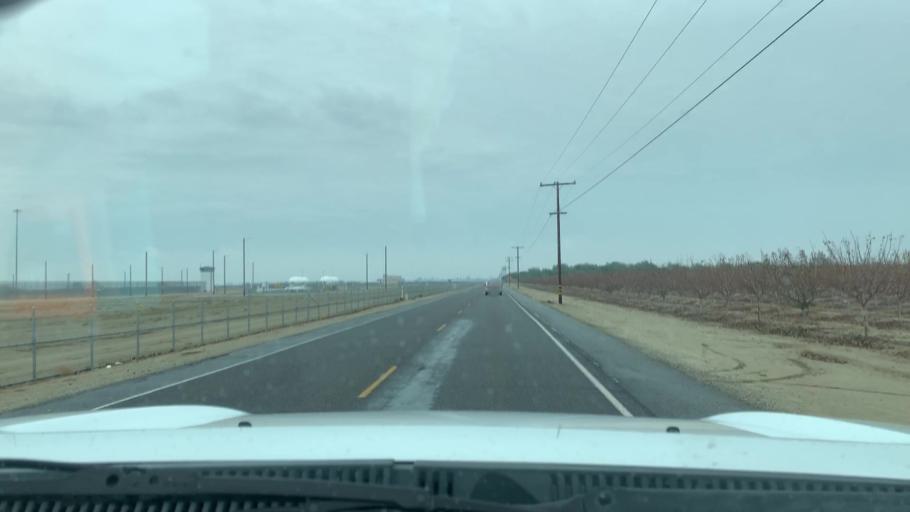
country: US
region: California
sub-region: Kern County
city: Delano
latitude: 35.7612
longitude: -119.3251
